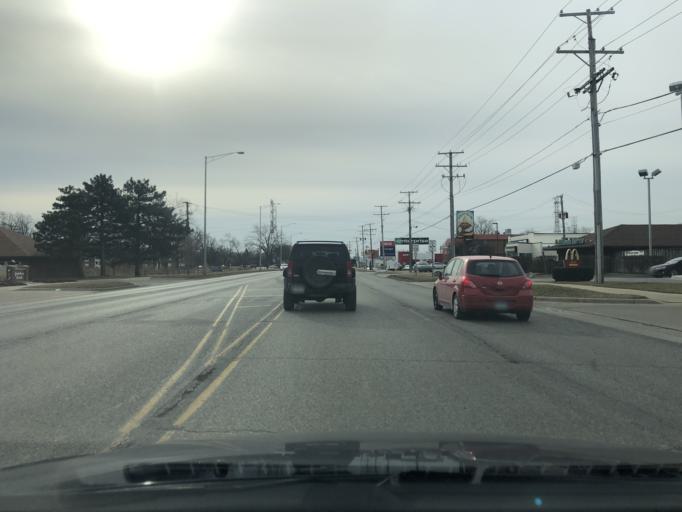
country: US
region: Illinois
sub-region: DuPage County
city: Bensenville
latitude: 41.9282
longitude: -87.9399
